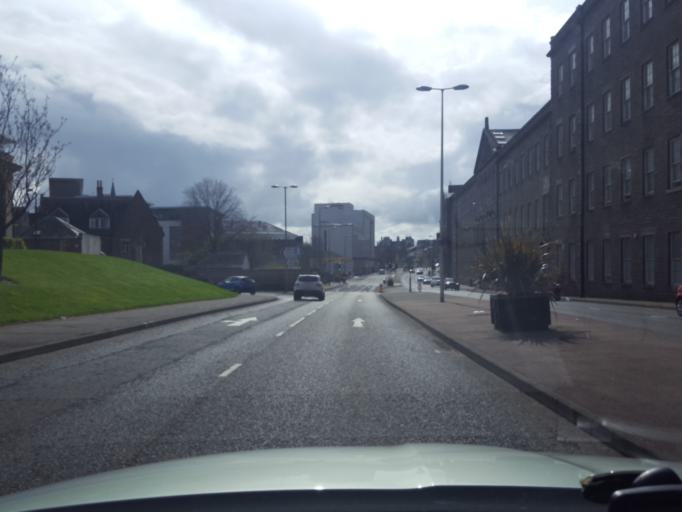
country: GB
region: Scotland
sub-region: Dundee City
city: Dundee
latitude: 56.4624
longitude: -2.9788
